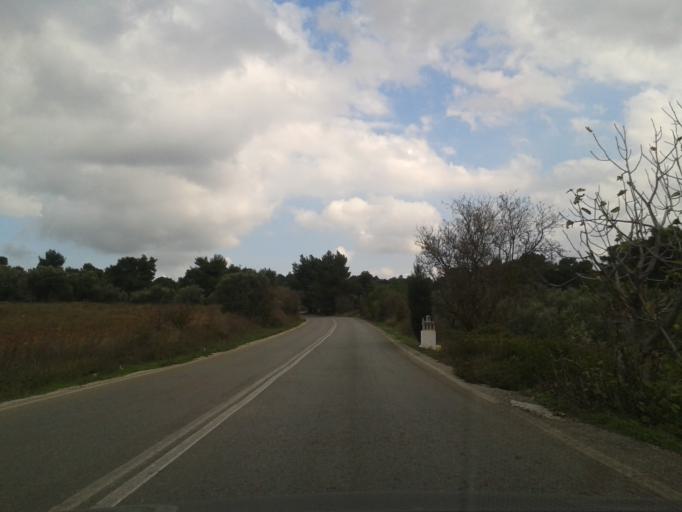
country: GR
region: Attica
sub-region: Nomarchia Anatolikis Attikis
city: Kapandriti
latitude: 38.2089
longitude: 23.8911
